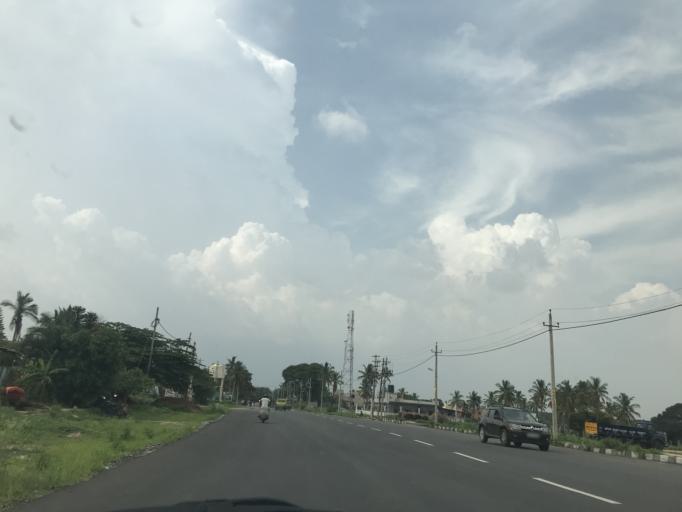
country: IN
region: Karnataka
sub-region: Bangalore Rural
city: Devanhalli
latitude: 13.1693
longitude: 77.6897
